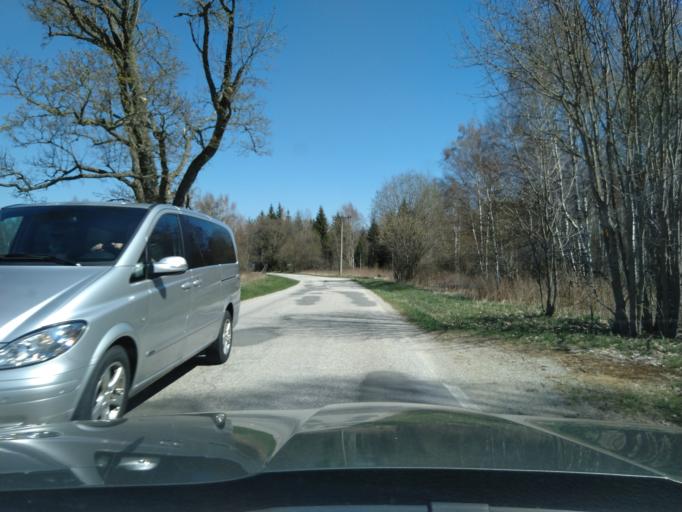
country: CZ
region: Jihocesky
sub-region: Okres Cesky Krumlov
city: Horni Plana
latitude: 48.7858
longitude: 13.9448
